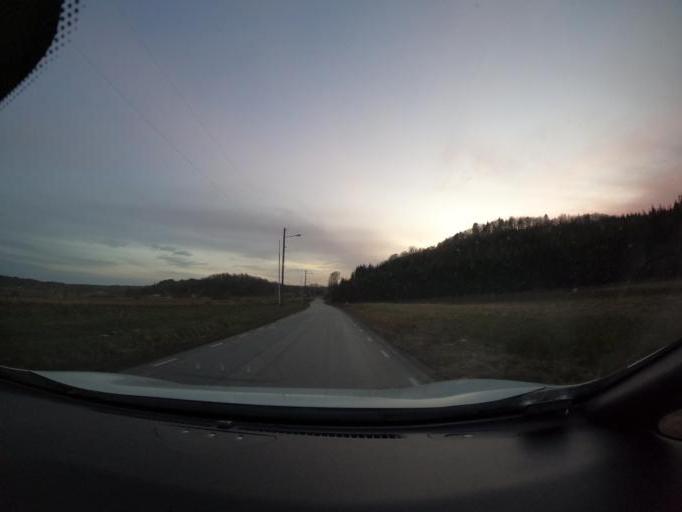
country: SE
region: Vaestra Goetaland
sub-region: Harryda Kommun
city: Molnlycke
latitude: 57.6056
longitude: 12.1388
